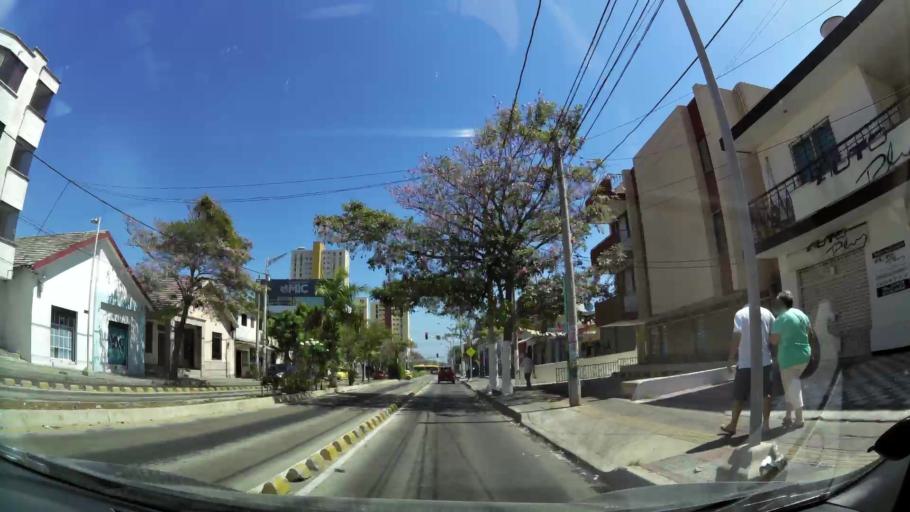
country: CO
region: Atlantico
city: Barranquilla
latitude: 10.9894
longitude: -74.7923
